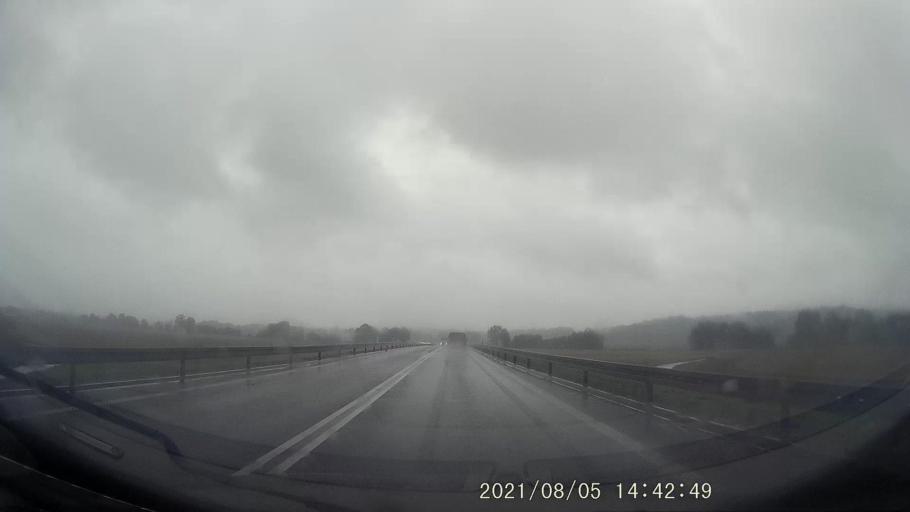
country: PL
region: Opole Voivodeship
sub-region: Powiat nyski
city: Nysa
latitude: 50.4775
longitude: 17.3989
